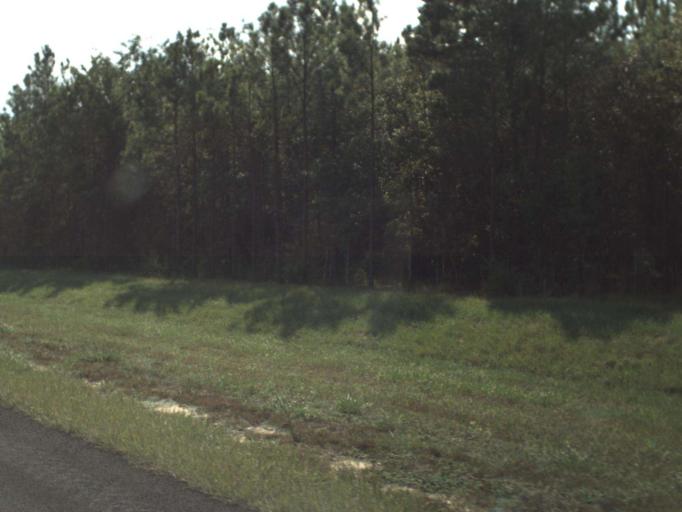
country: US
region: Florida
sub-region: Bay County
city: Laguna Beach
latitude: 30.4966
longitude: -85.8417
